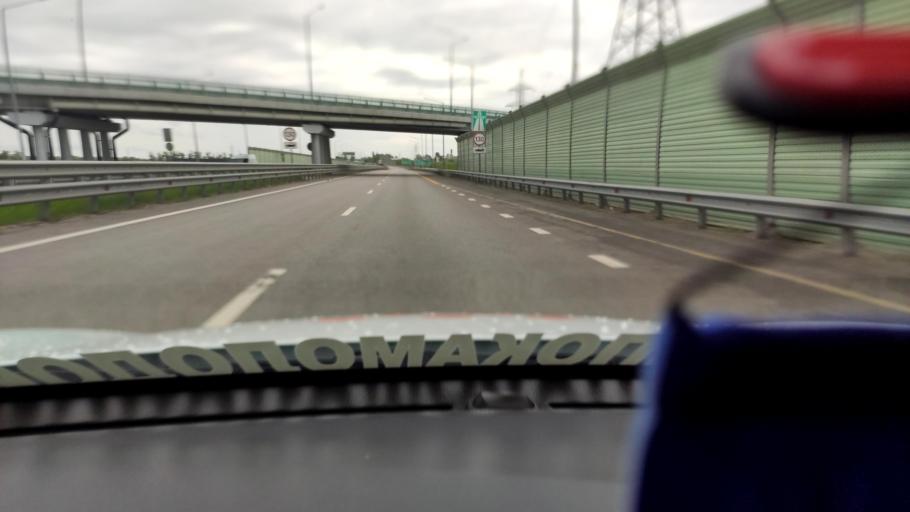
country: RU
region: Voronezj
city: Novaya Usman'
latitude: 51.6388
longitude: 39.3171
